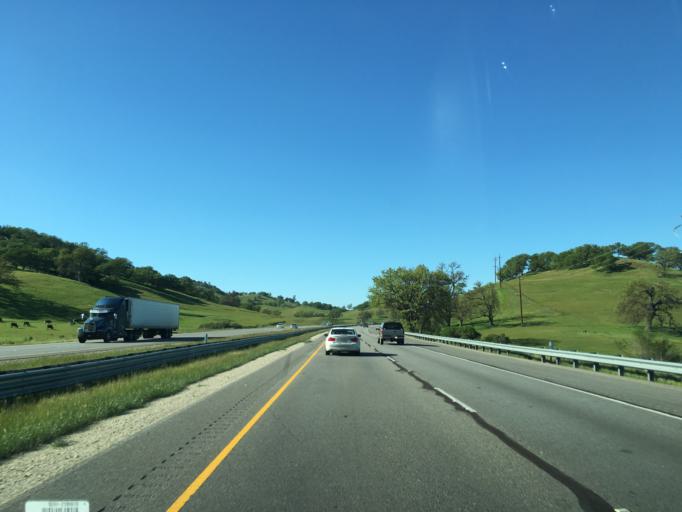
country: US
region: California
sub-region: San Luis Obispo County
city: Santa Margarita
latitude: 35.4050
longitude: -120.6244
